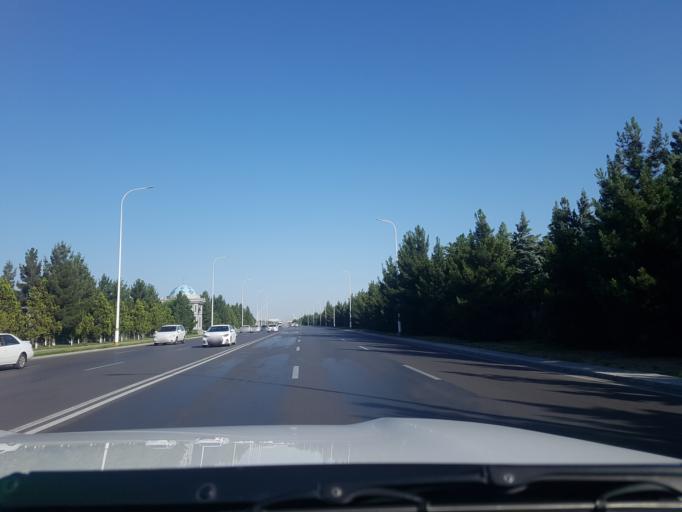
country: TM
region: Ahal
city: Abadan
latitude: 38.0223
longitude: 58.2491
